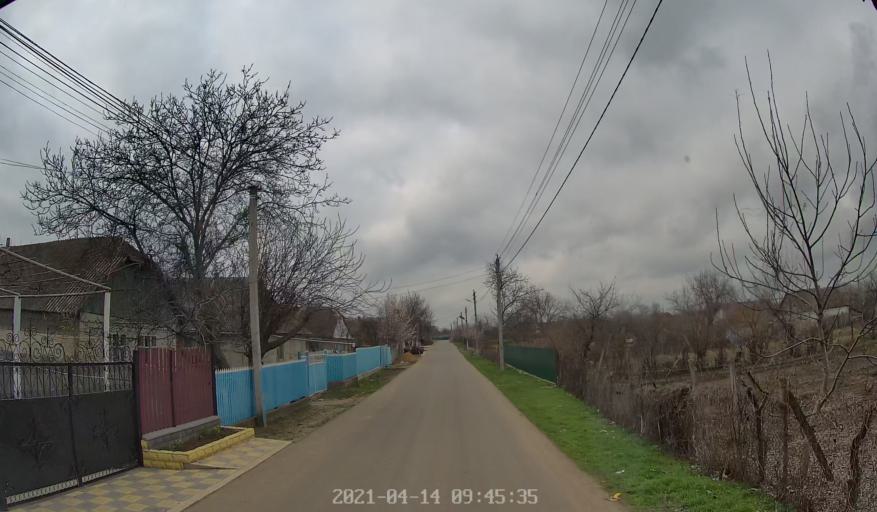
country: MD
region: Chisinau
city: Vadul lui Voda
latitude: 47.1354
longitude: 29.1269
